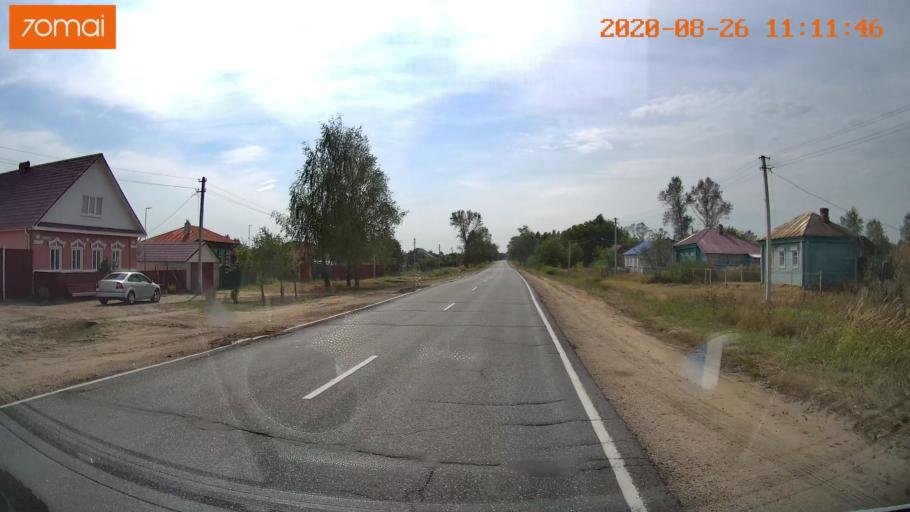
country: RU
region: Rjazan
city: Izhevskoye
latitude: 54.4767
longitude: 41.1260
